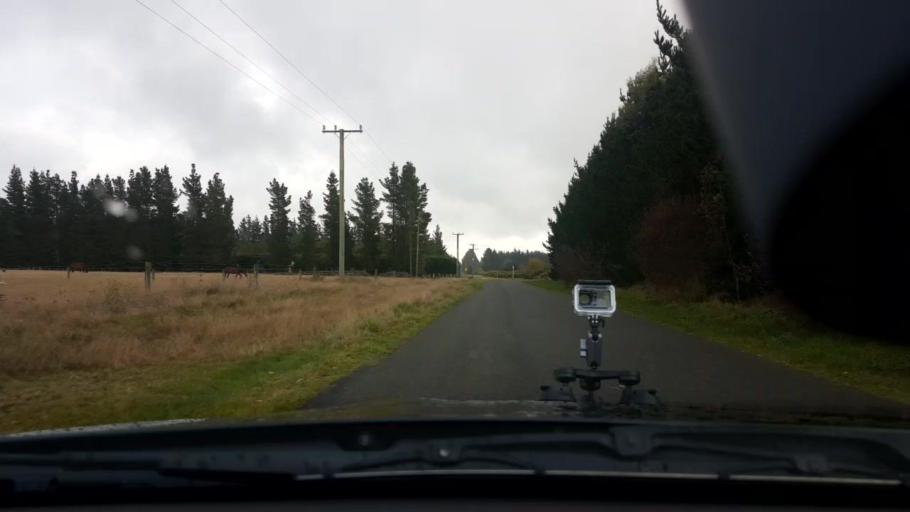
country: NZ
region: Canterbury
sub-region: Waimakariri District
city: Oxford
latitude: -43.3969
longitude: 172.3080
